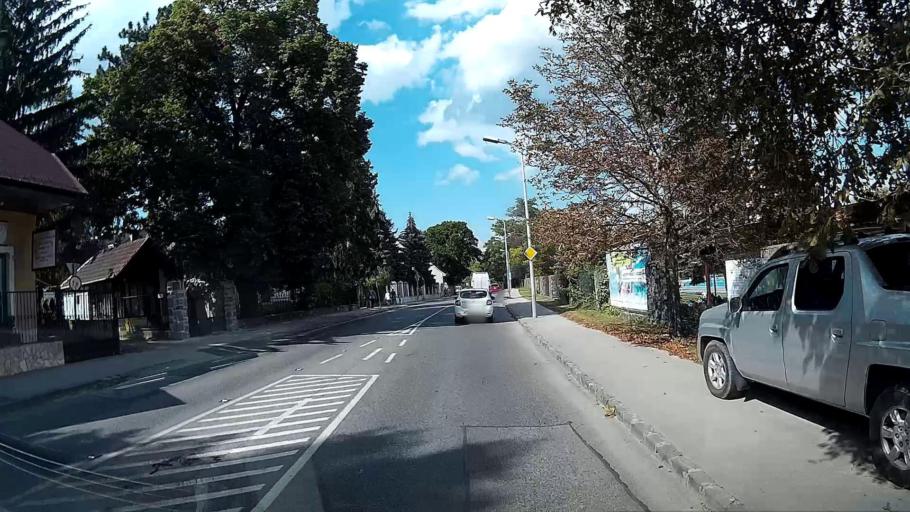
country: HU
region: Pest
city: Leanyfalu
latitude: 47.7207
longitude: 19.0890
